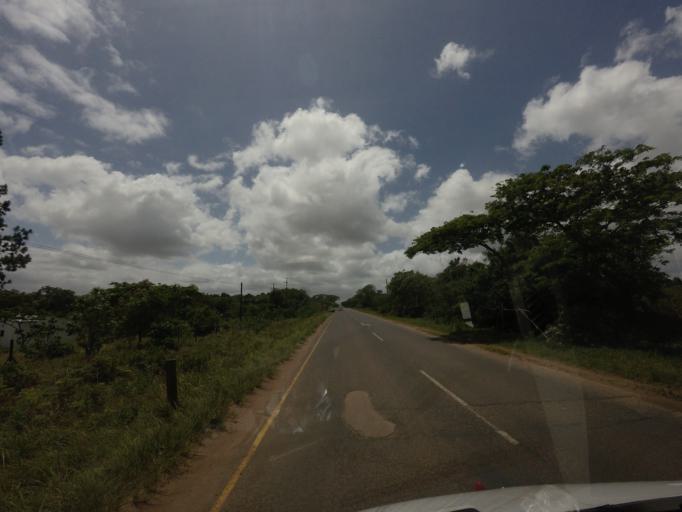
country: ZA
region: KwaZulu-Natal
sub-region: uMkhanyakude District Municipality
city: Mtubatuba
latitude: -28.3807
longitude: 32.3617
